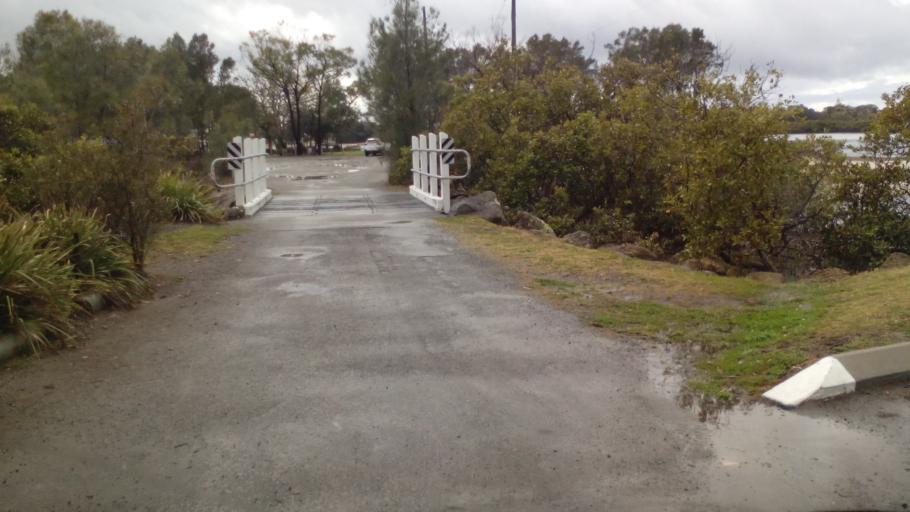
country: AU
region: New South Wales
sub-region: Lake Macquarie Shire
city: Belmont South
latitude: -33.0743
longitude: 151.6371
